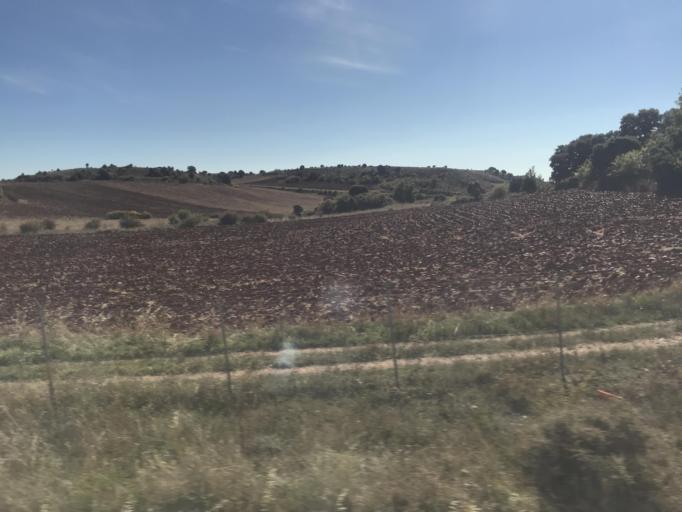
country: ES
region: Castille-La Mancha
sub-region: Provincia de Guadalajara
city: Sauca
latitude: 41.0041
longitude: -2.5045
